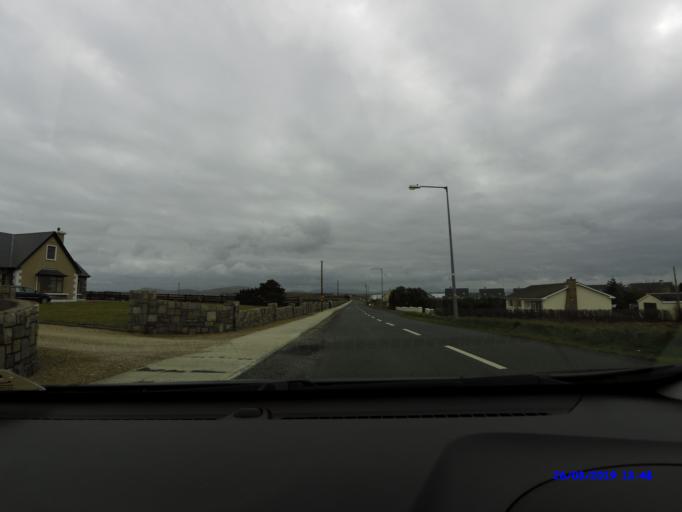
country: IE
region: Connaught
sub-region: Maigh Eo
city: Belmullet
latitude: 54.2178
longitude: -9.9824
